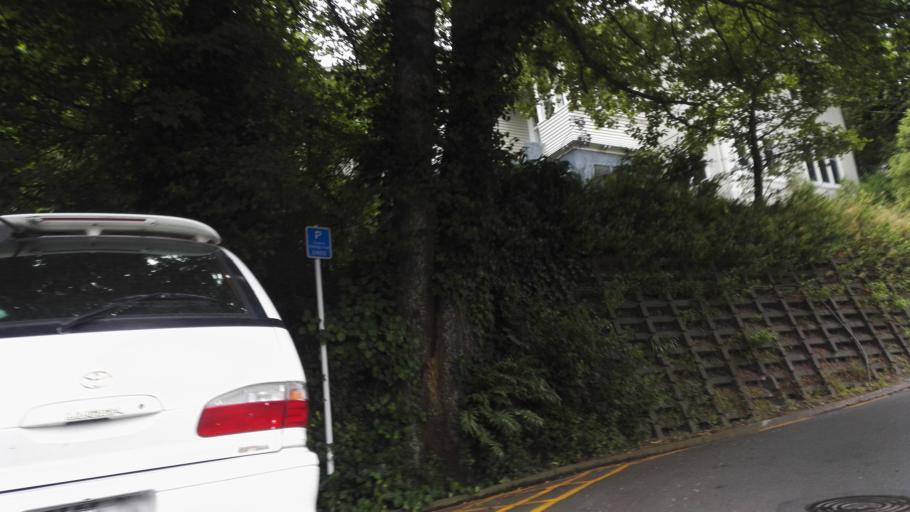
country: NZ
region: Wellington
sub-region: Wellington City
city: Wellington
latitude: -41.2947
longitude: 174.7690
